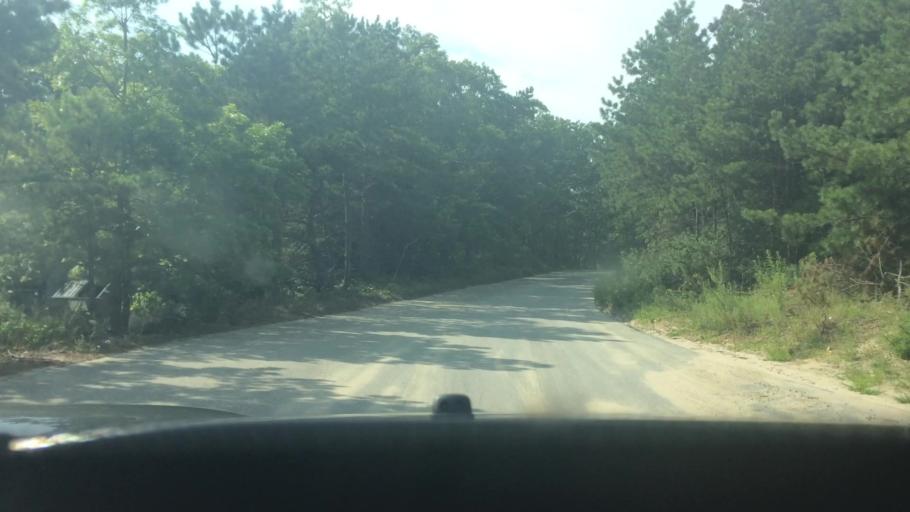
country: US
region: Massachusetts
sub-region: Barnstable County
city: Sandwich
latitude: 41.7268
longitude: -70.4890
